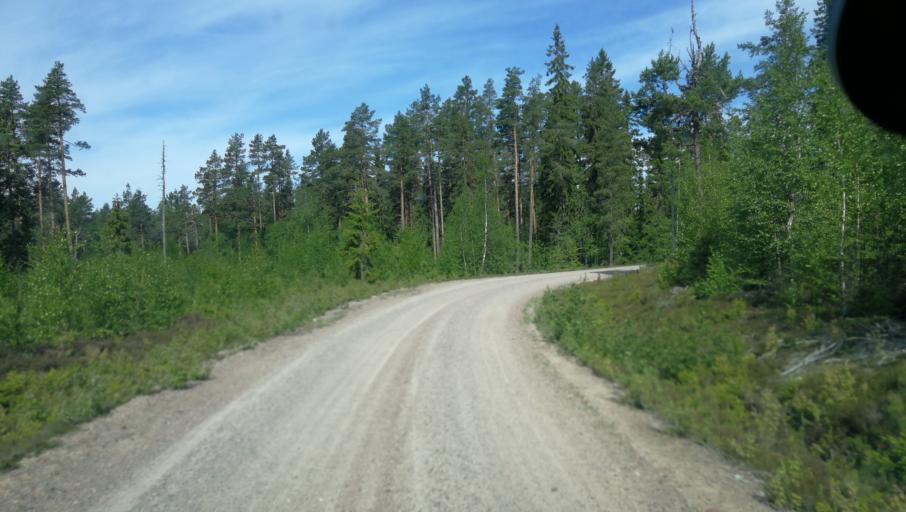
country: SE
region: Dalarna
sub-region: Vansbro Kommun
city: Vansbro
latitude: 60.8353
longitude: 14.1518
